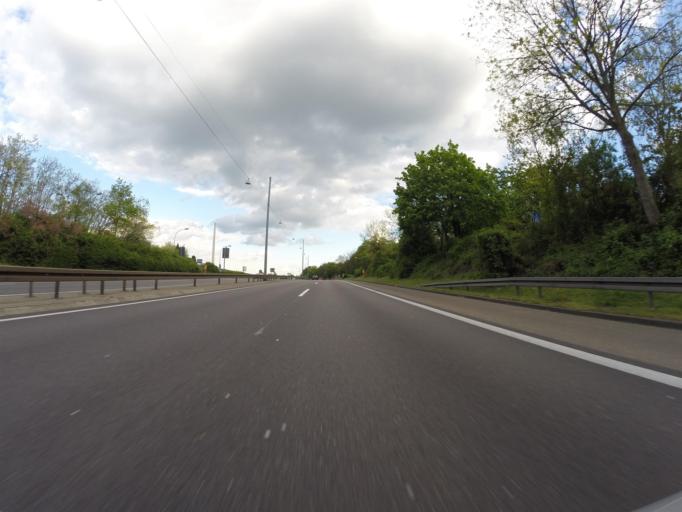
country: DE
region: Saarland
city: Saarbrucken
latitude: 49.2268
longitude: 7.0022
